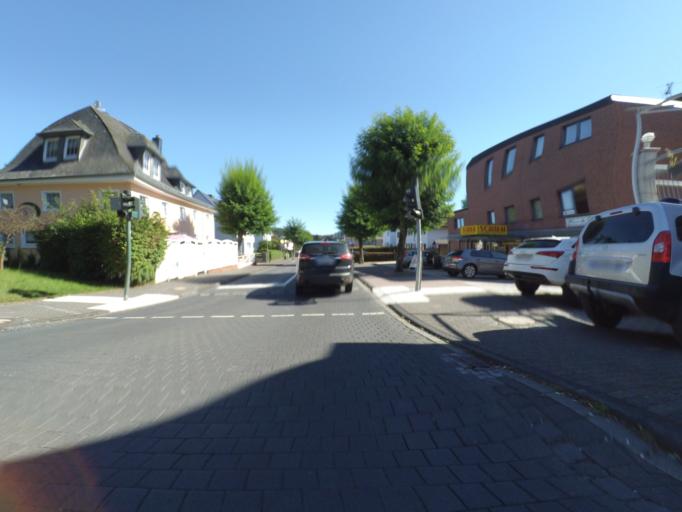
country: DE
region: Rheinland-Pfalz
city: Daun
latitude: 50.1973
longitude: 6.8274
